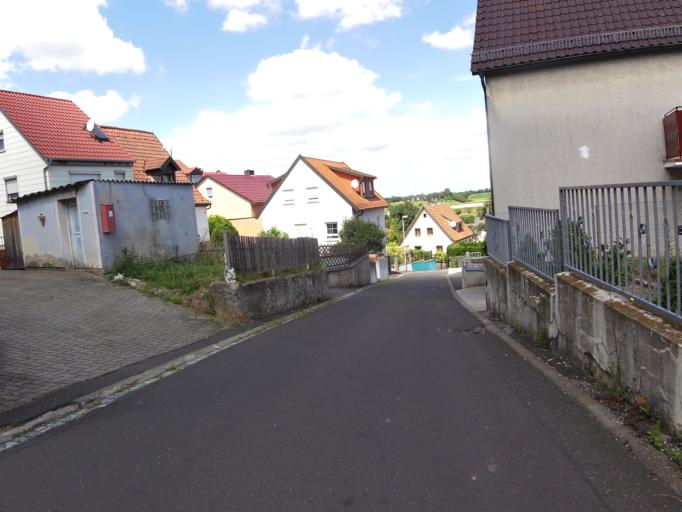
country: DE
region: Bavaria
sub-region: Regierungsbezirk Unterfranken
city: Kist
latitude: 49.7436
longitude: 9.8389
